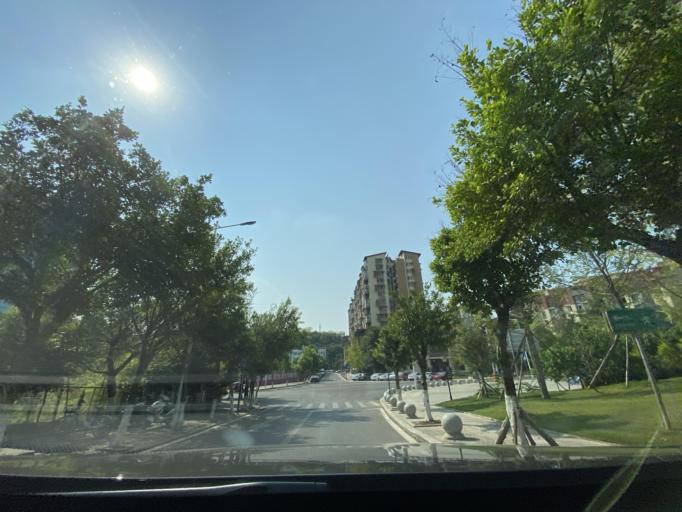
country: CN
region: Sichuan
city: Jiancheng
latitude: 30.4159
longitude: 104.5434
